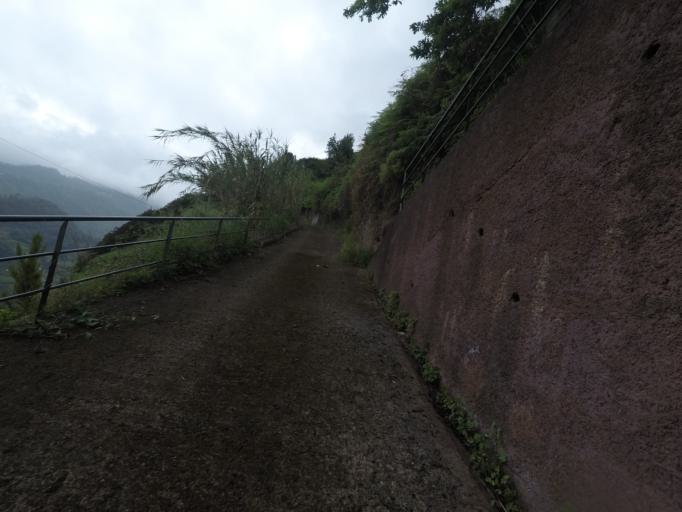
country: PT
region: Madeira
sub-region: Santana
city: Santana
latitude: 32.7697
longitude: -16.8754
